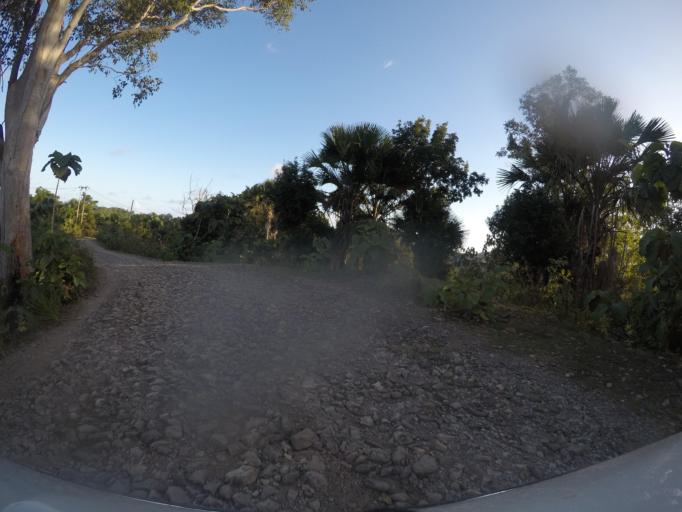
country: TL
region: Baucau
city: Venilale
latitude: -8.7190
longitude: 126.7121
